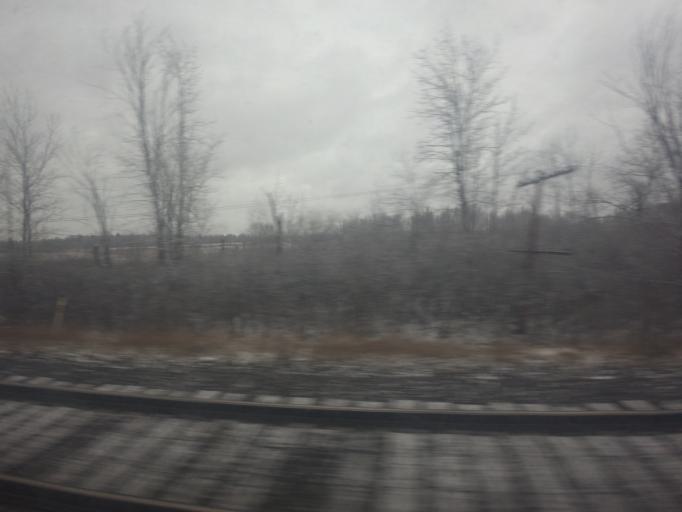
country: US
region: New York
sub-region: Jefferson County
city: Alexandria Bay
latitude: 44.4135
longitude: -76.0007
